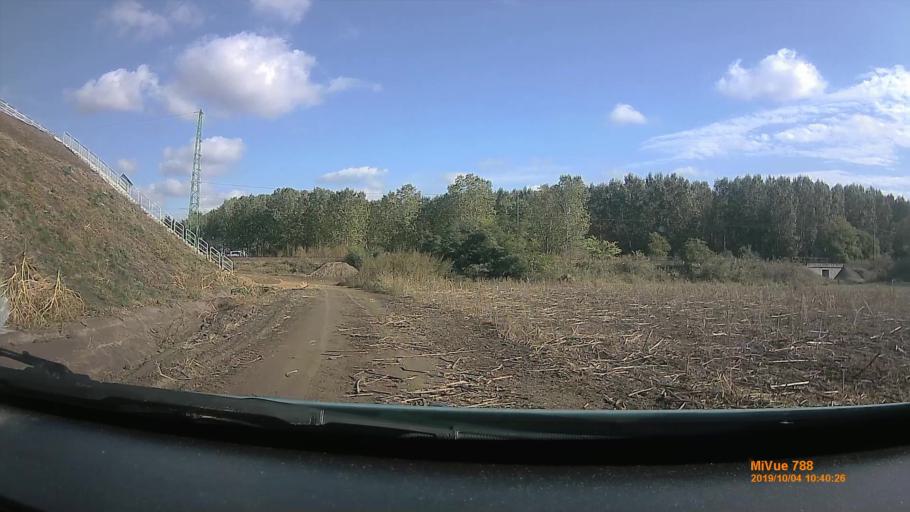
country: HU
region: Szabolcs-Szatmar-Bereg
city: Nyirtelek
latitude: 47.9790
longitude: 21.6638
